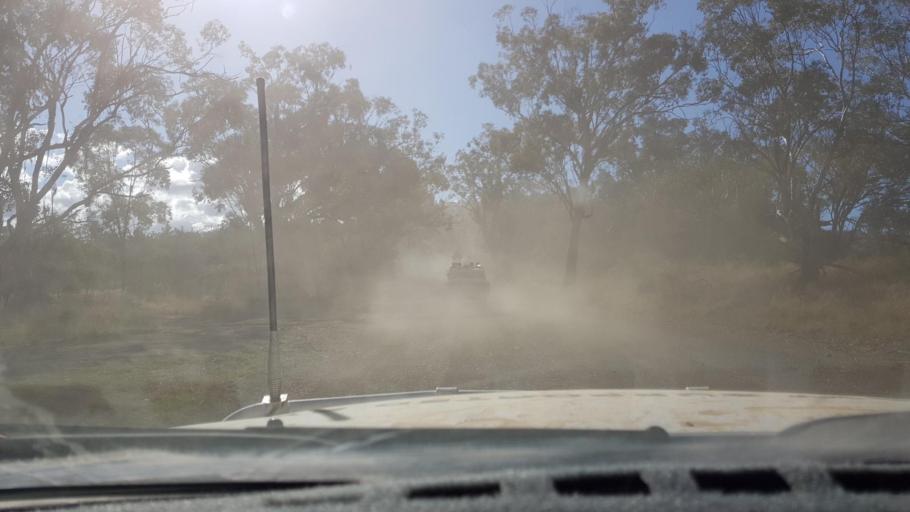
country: AU
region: New South Wales
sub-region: Tamworth Municipality
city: Manilla
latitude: -30.6551
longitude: 150.4894
